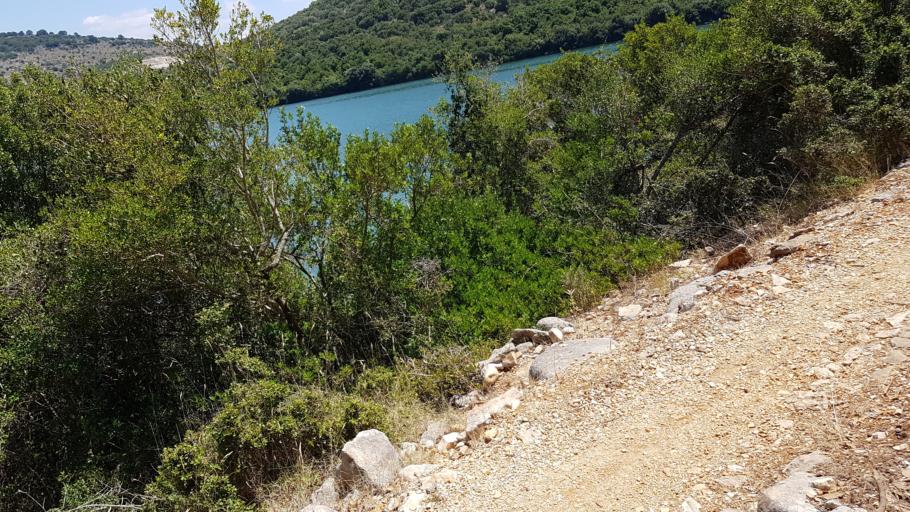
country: AL
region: Vlore
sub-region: Rrethi i Sarandes
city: Xarre
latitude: 39.7505
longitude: 19.9950
